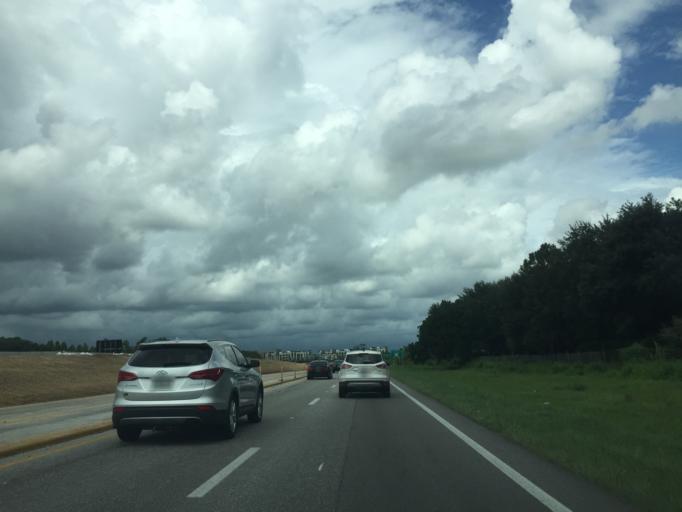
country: US
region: Florida
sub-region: Orange County
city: Eatonville
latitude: 28.6369
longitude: -81.4034
